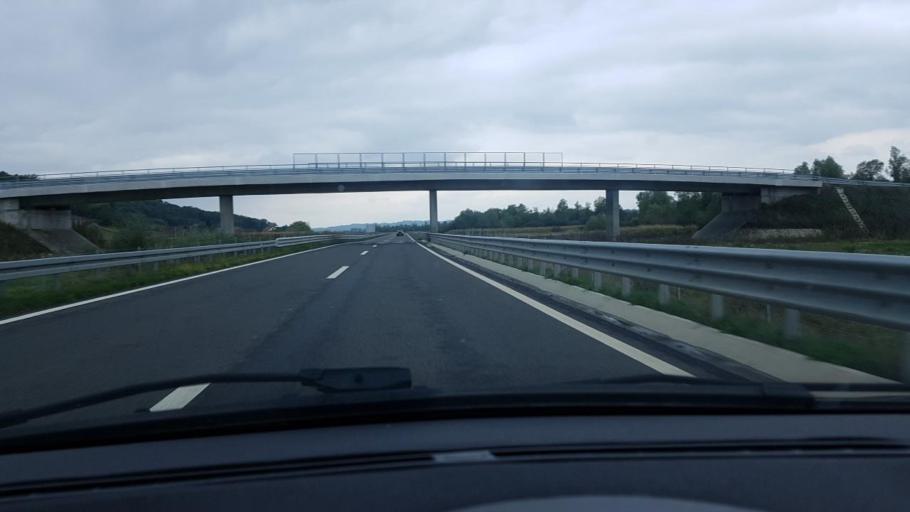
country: HR
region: Krapinsko-Zagorska
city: Selnica
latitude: 46.0395
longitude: 16.0510
